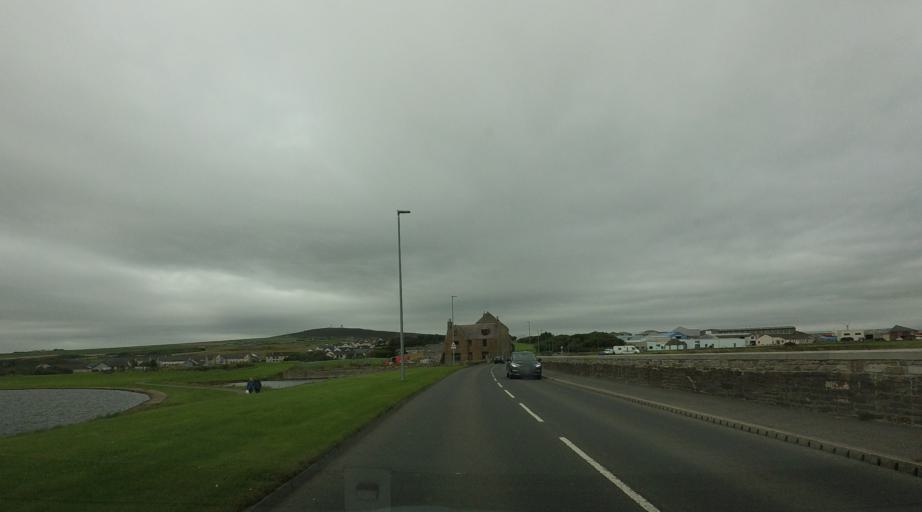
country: GB
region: Scotland
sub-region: Orkney Islands
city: Orkney
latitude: 58.9851
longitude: -2.9665
